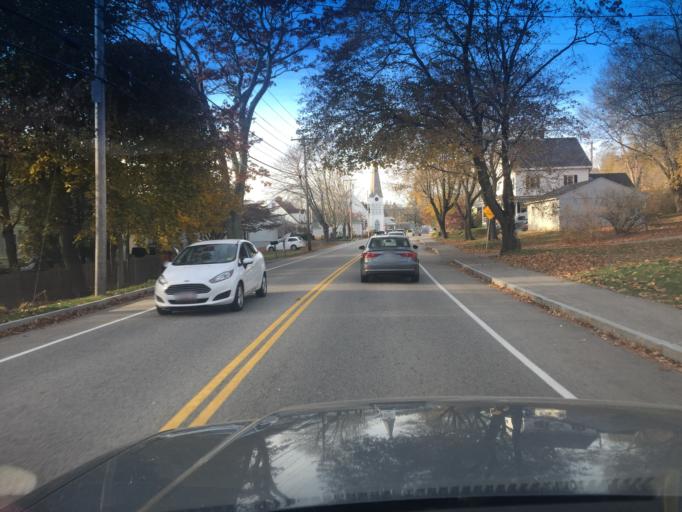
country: US
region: Maine
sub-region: York County
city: York Harbor
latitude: 43.1471
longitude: -70.6604
